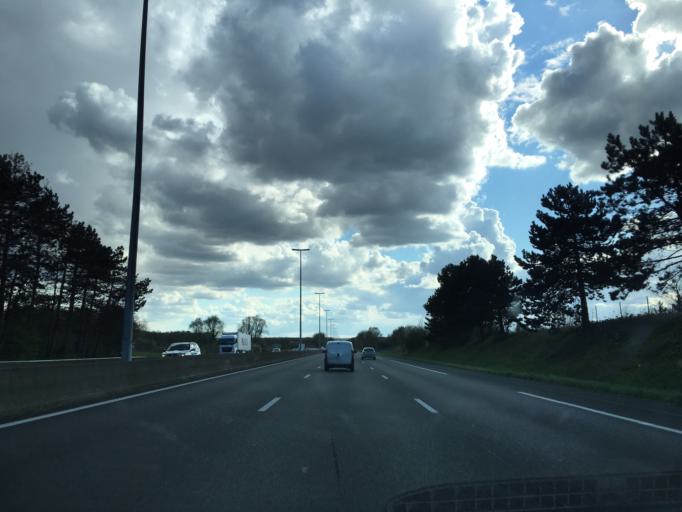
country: FR
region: Picardie
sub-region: Departement de l'Oise
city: Thiers-sur-Theve
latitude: 49.1559
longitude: 2.5903
